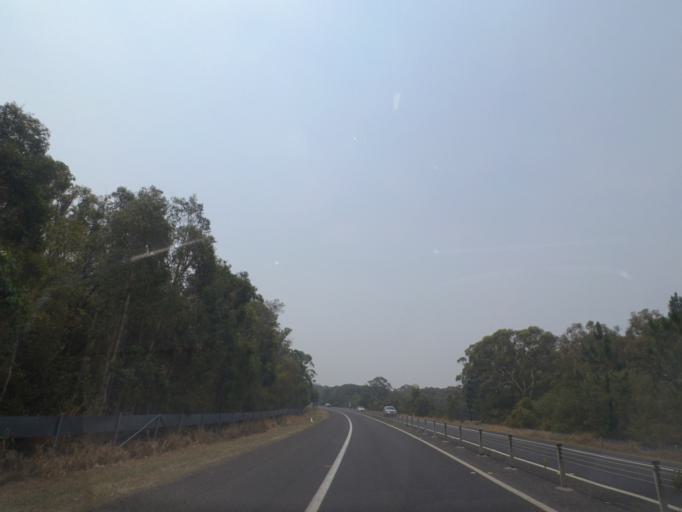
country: AU
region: New South Wales
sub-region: Ballina
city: Ballina
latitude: -28.9300
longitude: 153.4749
